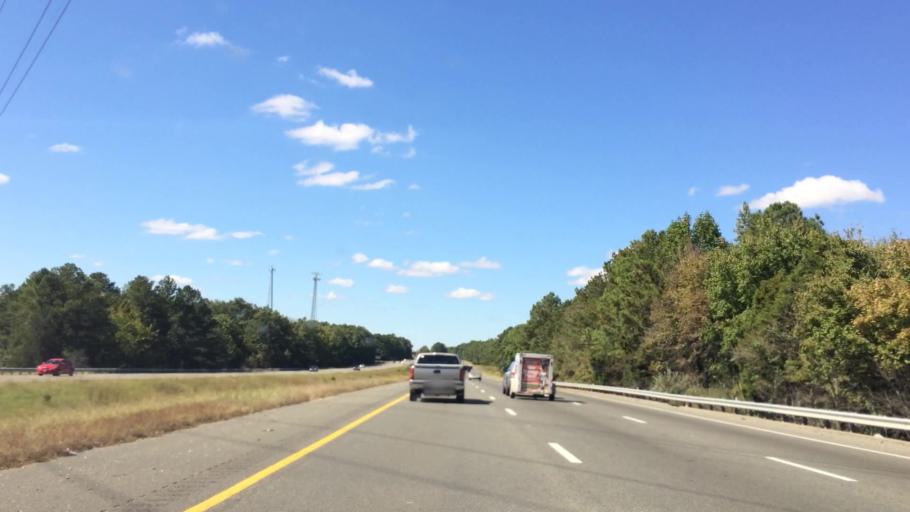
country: US
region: Virginia
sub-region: Henrico County
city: Glen Allen
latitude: 37.6773
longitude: -77.5044
